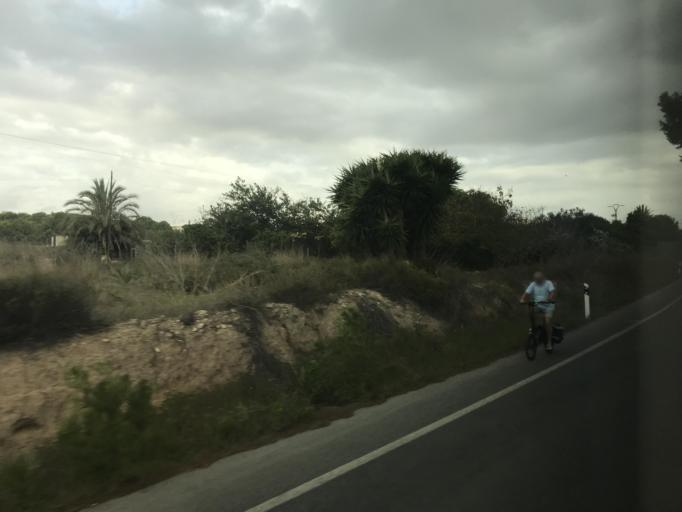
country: ES
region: Valencia
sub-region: Provincia de Alicante
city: Guardamar del Segura
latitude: 38.1275
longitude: -0.6506
